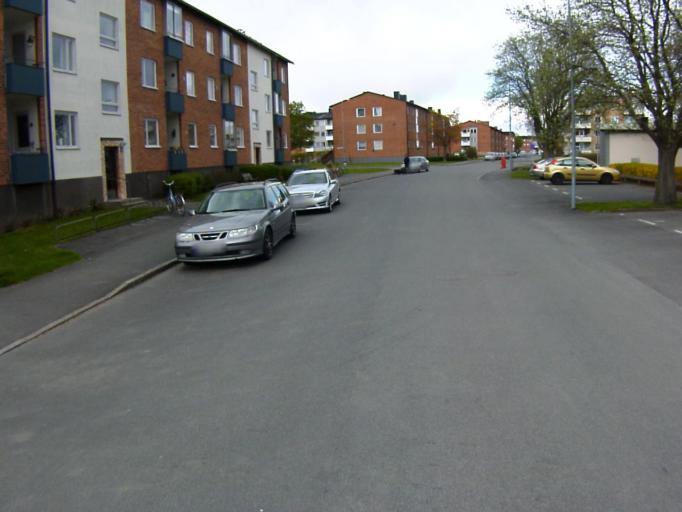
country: SE
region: Skane
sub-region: Kristianstads Kommun
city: Kristianstad
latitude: 56.0426
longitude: 14.1630
